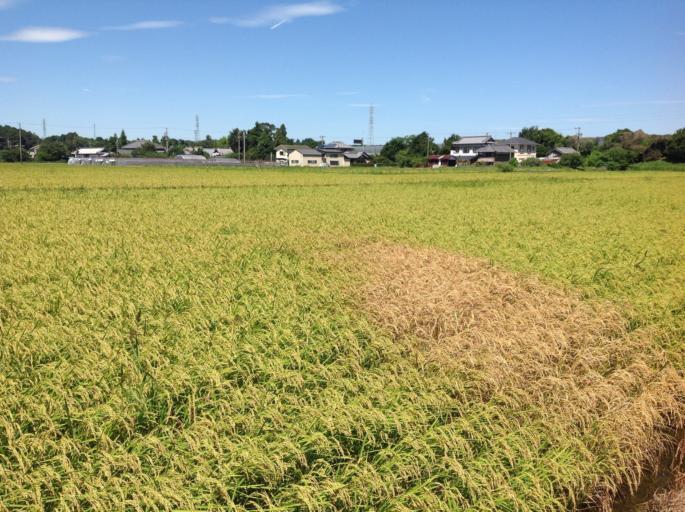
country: JP
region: Shizuoka
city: Kakegawa
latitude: 34.7674
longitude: 137.9669
